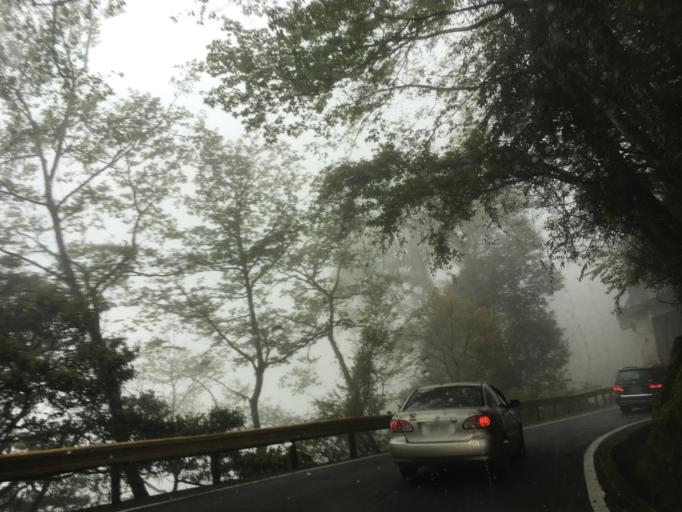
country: TW
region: Taiwan
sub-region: Hualien
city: Hualian
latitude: 24.1877
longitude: 121.4129
